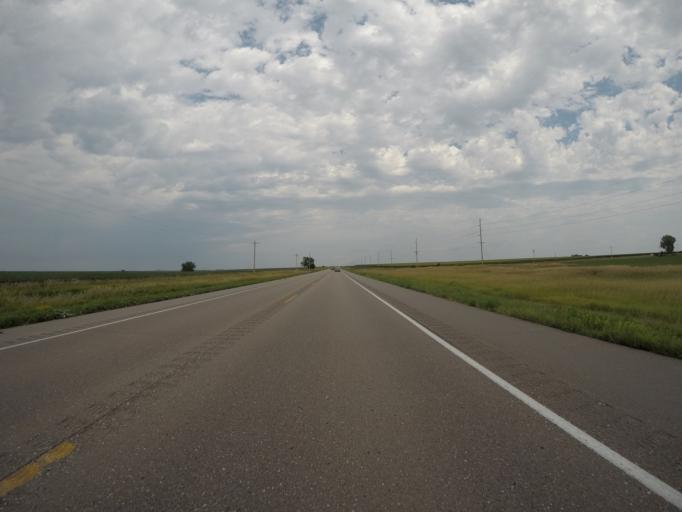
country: US
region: Nebraska
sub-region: Clay County
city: Harvard
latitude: 40.5827
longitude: -98.1491
